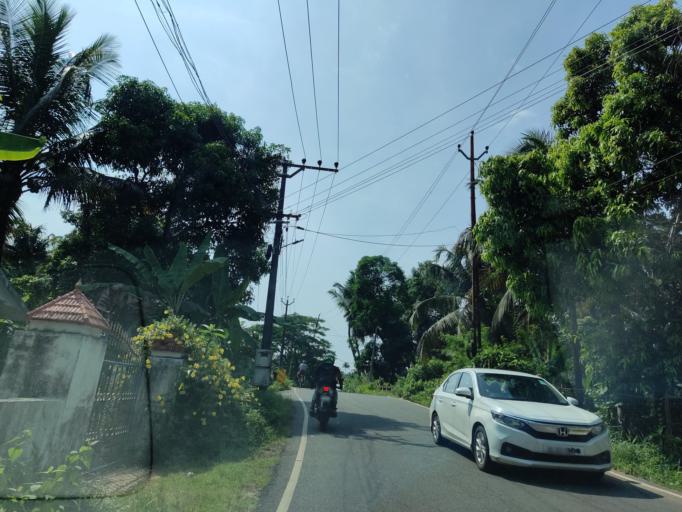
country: IN
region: Kerala
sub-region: Pattanamtitta
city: Tiruvalla
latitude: 9.3550
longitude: 76.4686
